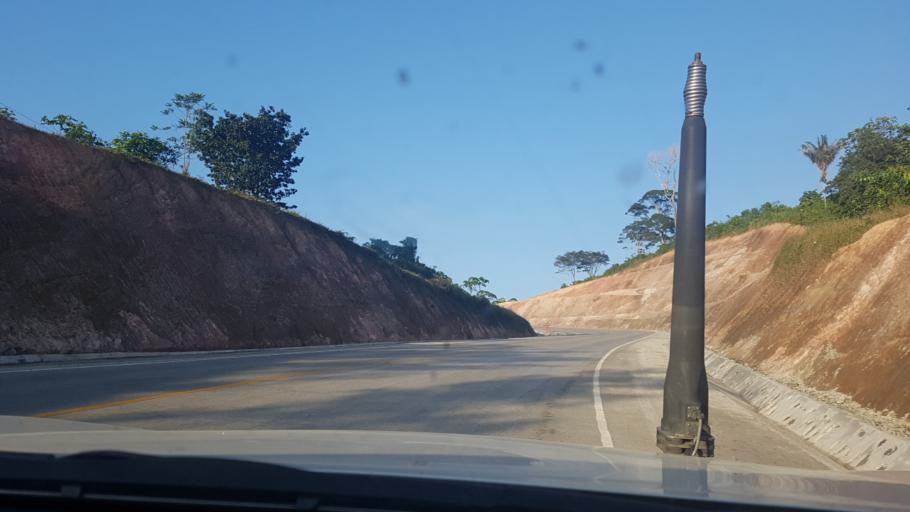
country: NI
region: Atlantico Sur
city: Rama
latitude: 11.8286
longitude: -84.0820
